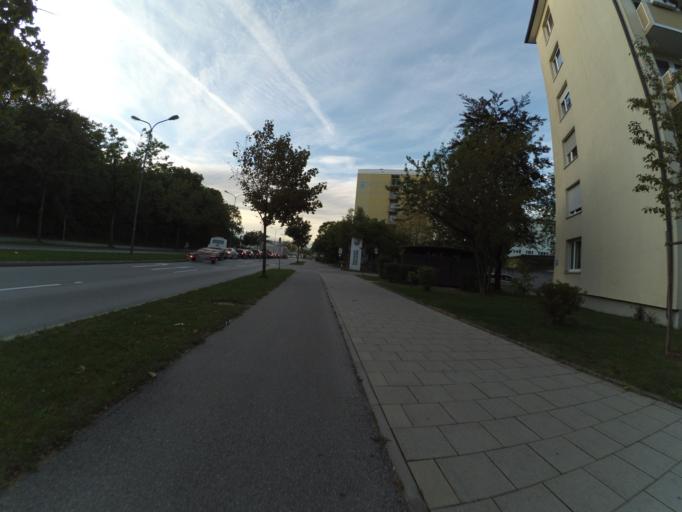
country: DE
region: Bavaria
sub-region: Upper Bavaria
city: Munich
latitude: 48.1849
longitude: 11.5528
